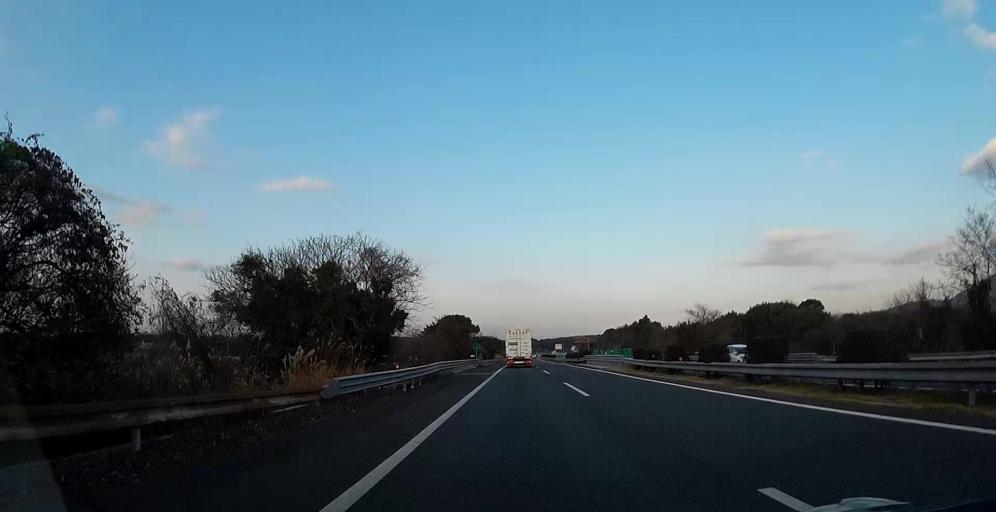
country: JP
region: Kumamoto
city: Kumamoto
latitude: 32.7370
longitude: 130.7793
